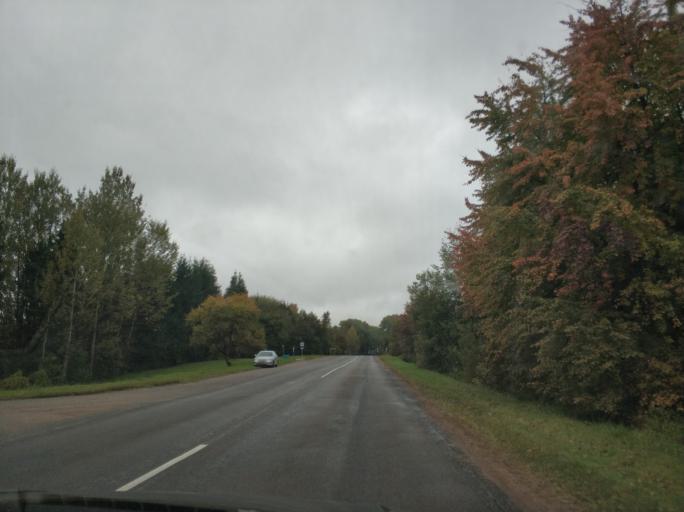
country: BY
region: Vitebsk
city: Polatsk
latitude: 55.4439
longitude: 28.9470
